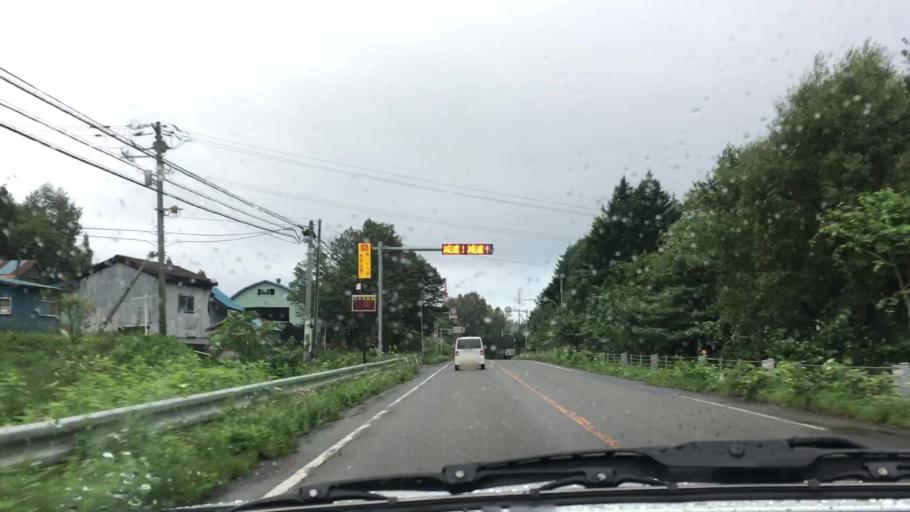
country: JP
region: Hokkaido
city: Niseko Town
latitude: 42.5982
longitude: 140.7224
